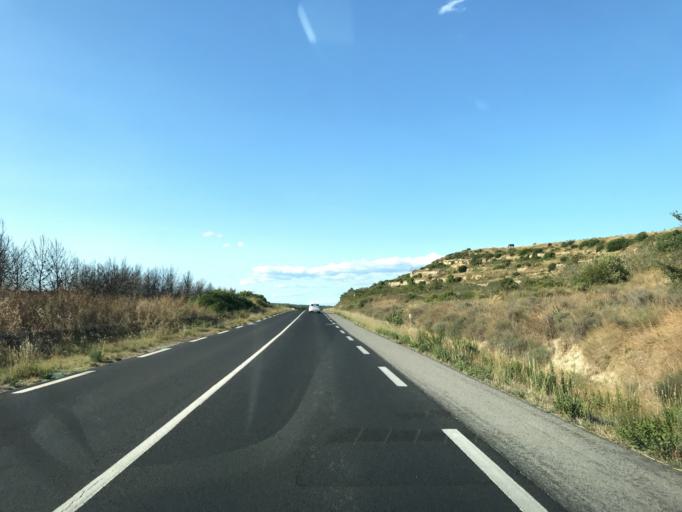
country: FR
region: Languedoc-Roussillon
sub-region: Departement de l'Herault
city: Montbazin
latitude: 43.5044
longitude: 3.6840
